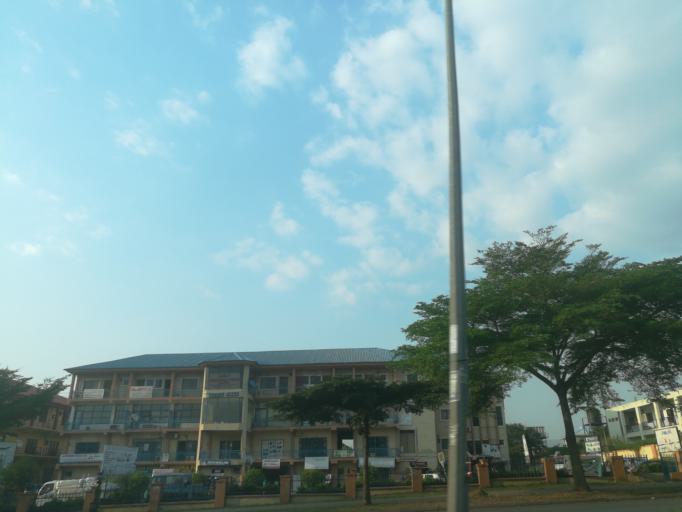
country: NG
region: Abuja Federal Capital Territory
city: Abuja
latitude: 9.0672
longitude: 7.4384
